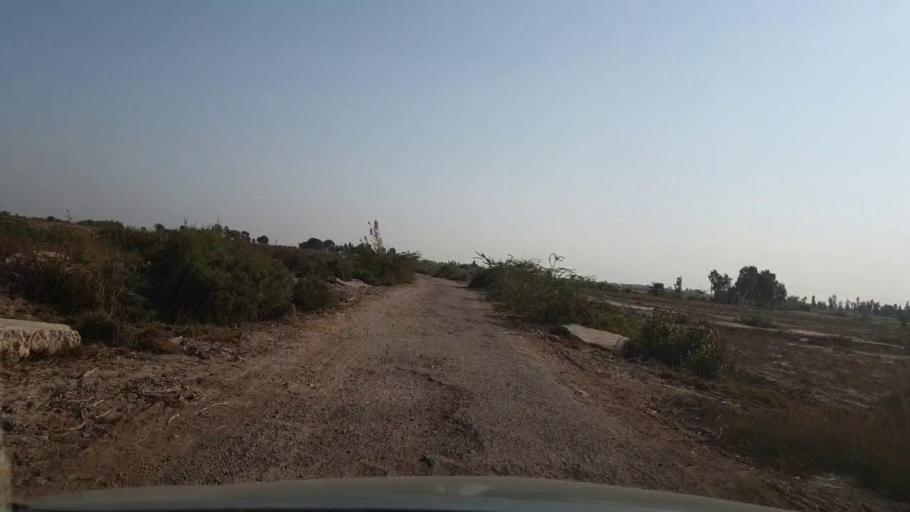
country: PK
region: Sindh
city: Tando Allahyar
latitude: 25.5987
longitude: 68.6259
